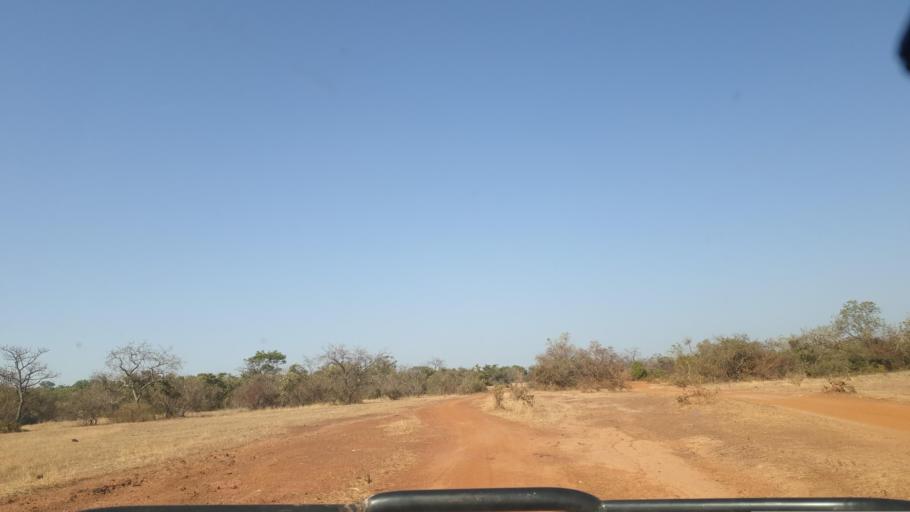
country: ML
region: Sikasso
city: Bougouni
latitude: 11.8190
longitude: -6.9465
